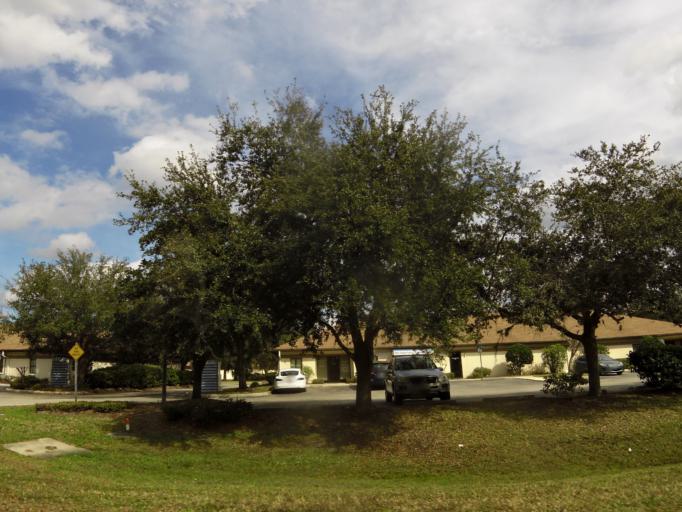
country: US
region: Florida
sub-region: Flagler County
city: Palm Coast
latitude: 29.5523
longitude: -81.2336
